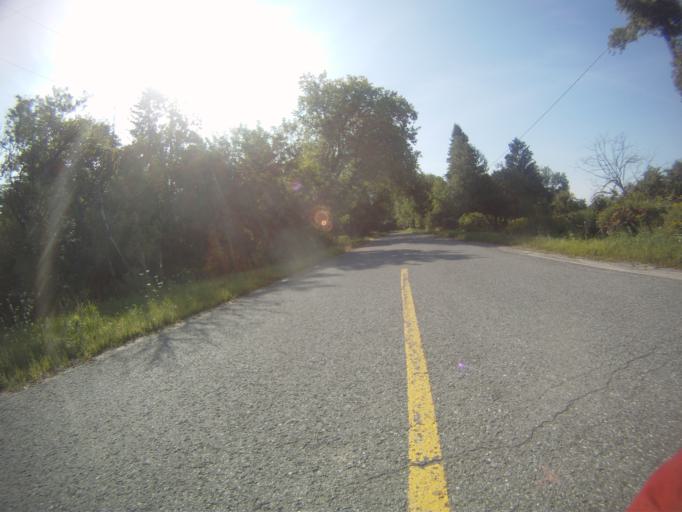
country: CA
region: Ontario
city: Bells Corners
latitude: 45.3421
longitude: -75.8870
